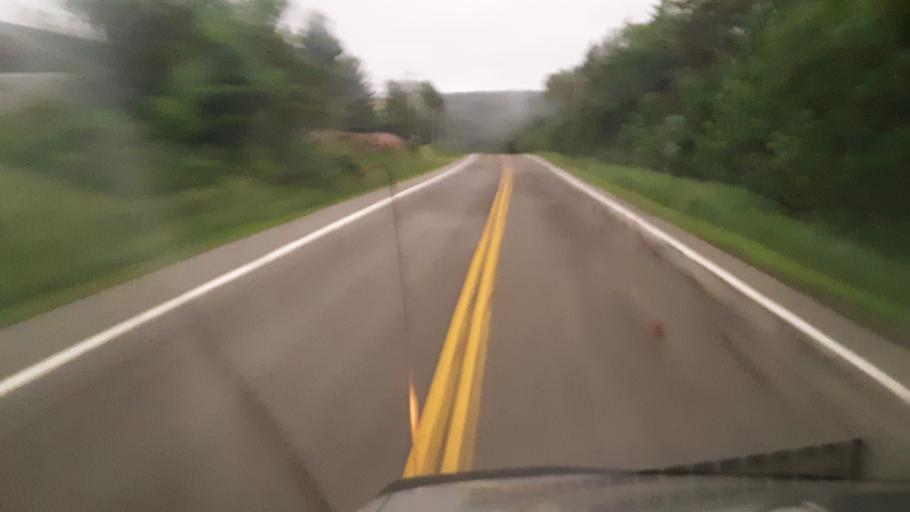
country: US
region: Maine
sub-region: Penobscot County
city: Patten
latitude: 46.0587
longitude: -68.4400
